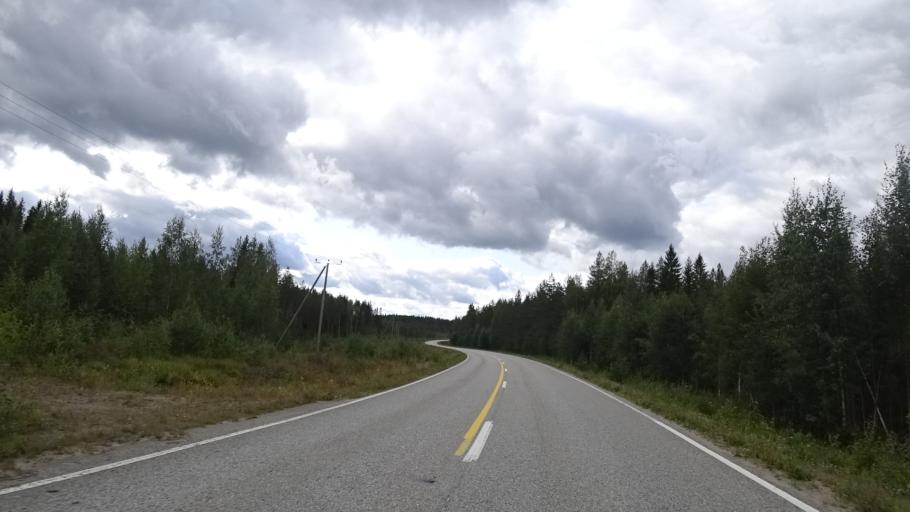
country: FI
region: North Karelia
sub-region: Joensuu
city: Ilomantsi
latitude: 62.6242
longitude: 31.2422
